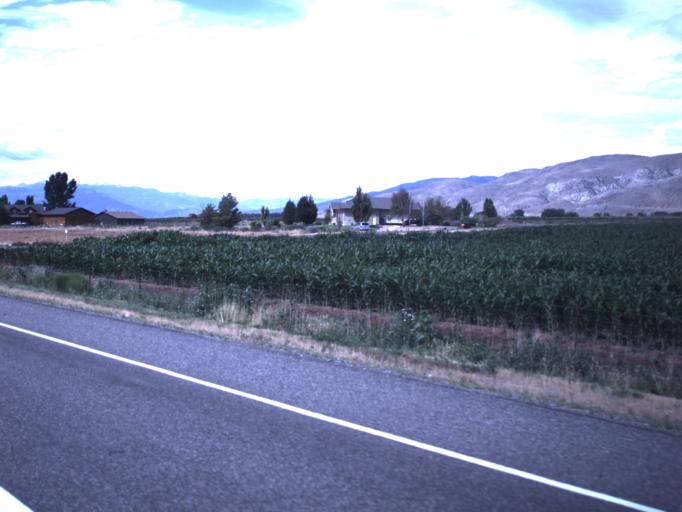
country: US
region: Utah
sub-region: Sevier County
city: Richfield
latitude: 38.7037
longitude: -112.1099
